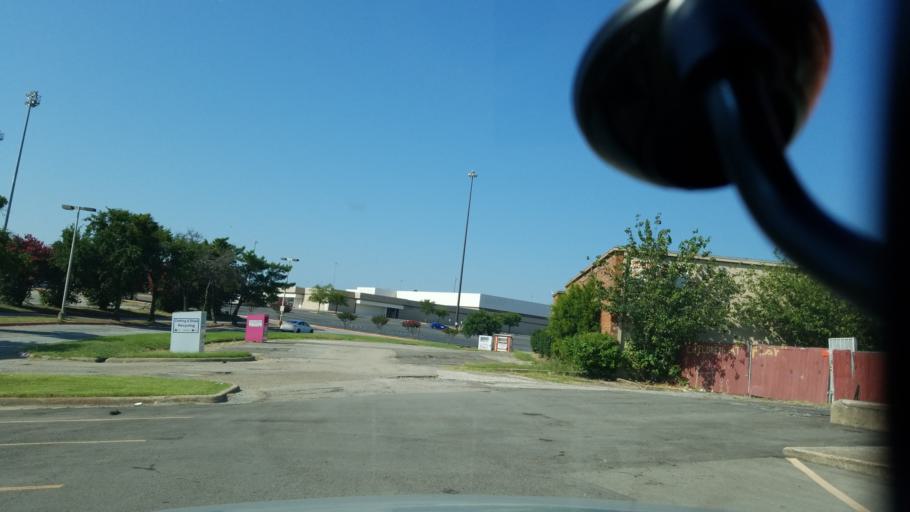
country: US
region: Texas
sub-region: Dallas County
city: Duncanville
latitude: 32.6622
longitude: -96.8746
